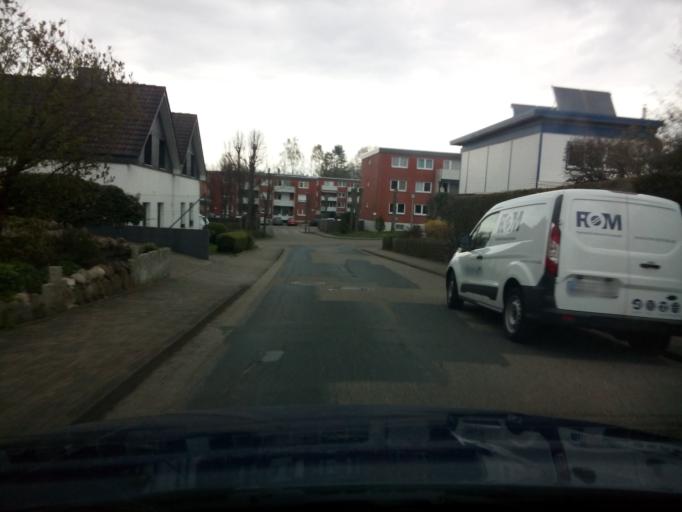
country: DE
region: Lower Saxony
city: Osterholz-Scharmbeck
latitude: 53.2401
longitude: 8.7796
